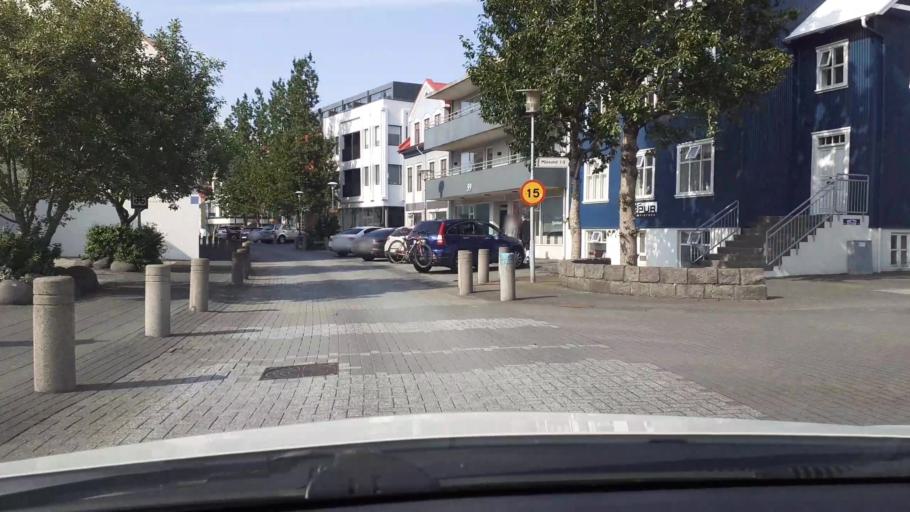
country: IS
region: Capital Region
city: Hafnarfjoerdur
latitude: 64.0675
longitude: -21.9546
